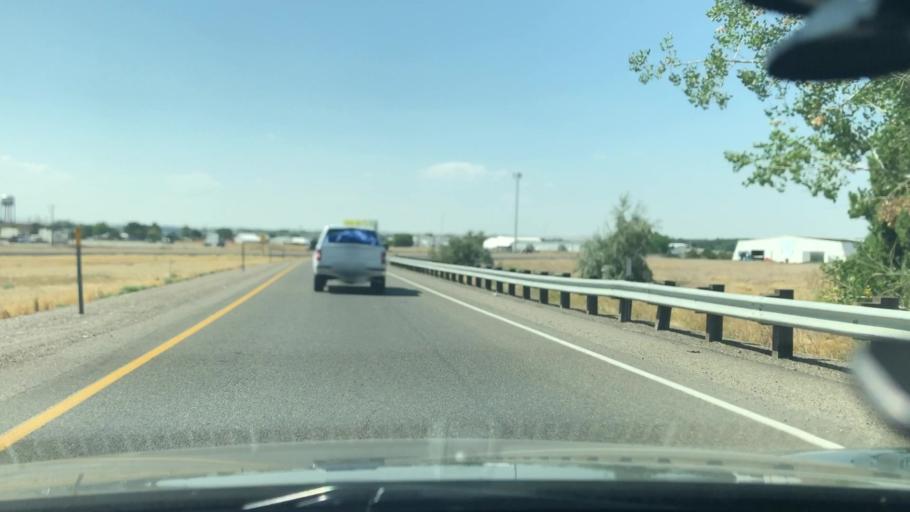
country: US
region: Oregon
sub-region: Malheur County
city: Ontario
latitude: 44.0263
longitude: -116.9479
